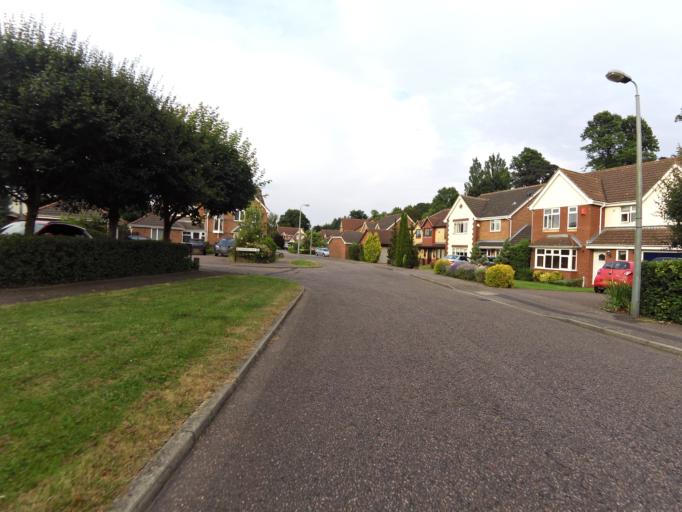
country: GB
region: England
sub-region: Suffolk
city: Ipswich
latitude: 52.0688
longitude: 1.1710
